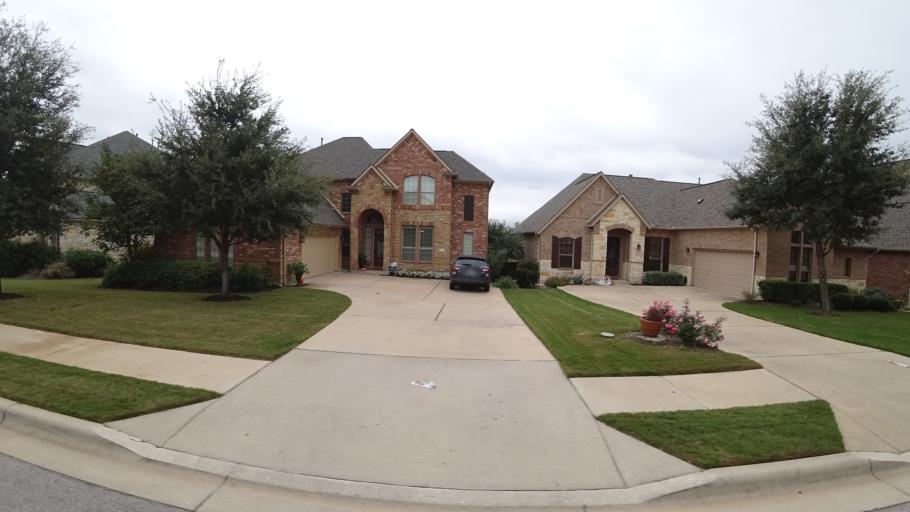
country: US
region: Texas
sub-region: Travis County
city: Bee Cave
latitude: 30.3427
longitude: -97.9091
